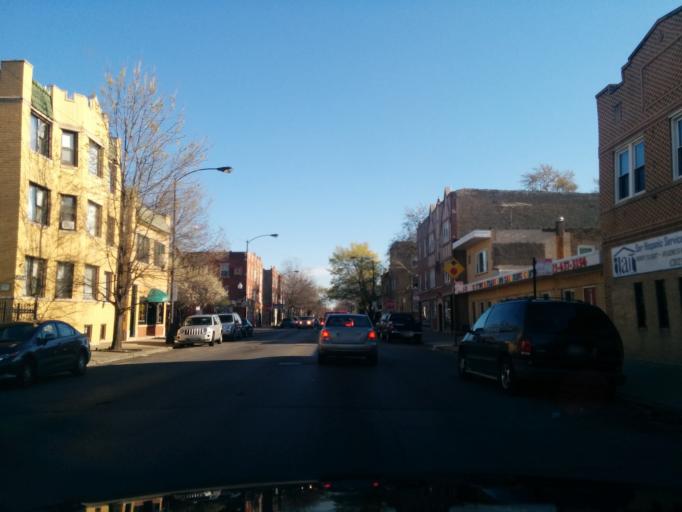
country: US
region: Illinois
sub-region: Cook County
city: Oak Park
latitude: 41.9302
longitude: -87.7564
